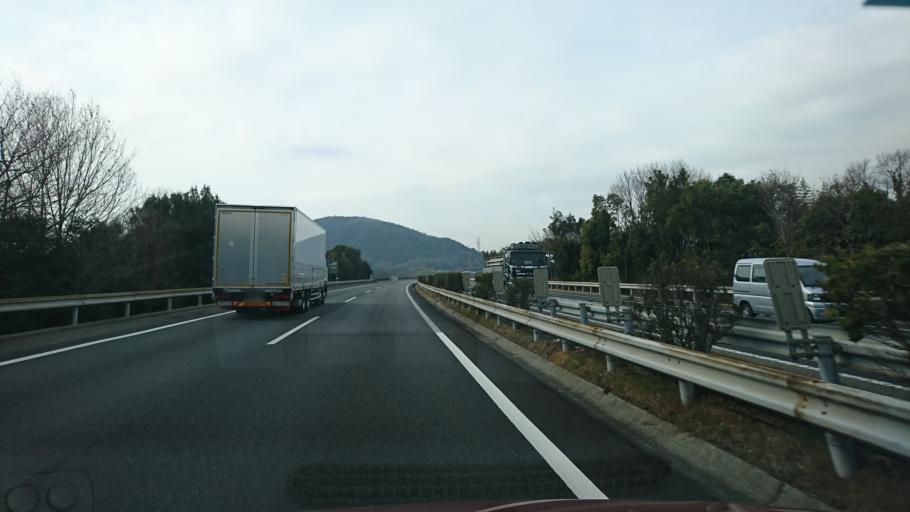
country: JP
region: Okayama
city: Kamogatacho-kamogata
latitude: 34.5387
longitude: 133.5630
